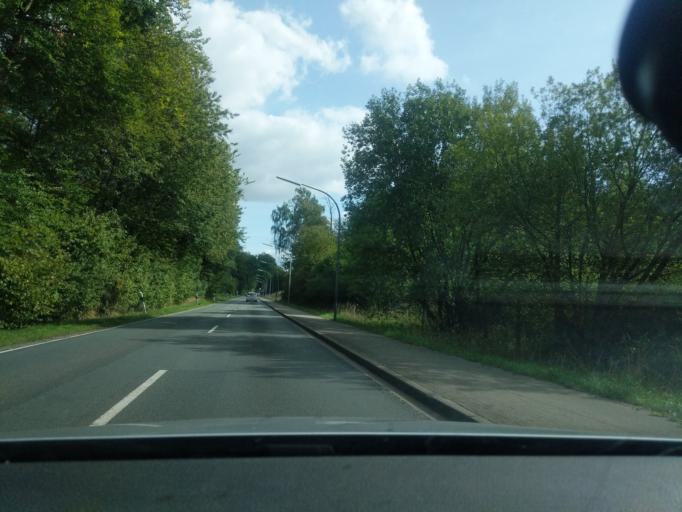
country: DE
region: Lower Saxony
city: Belm
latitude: 52.3096
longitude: 8.0930
